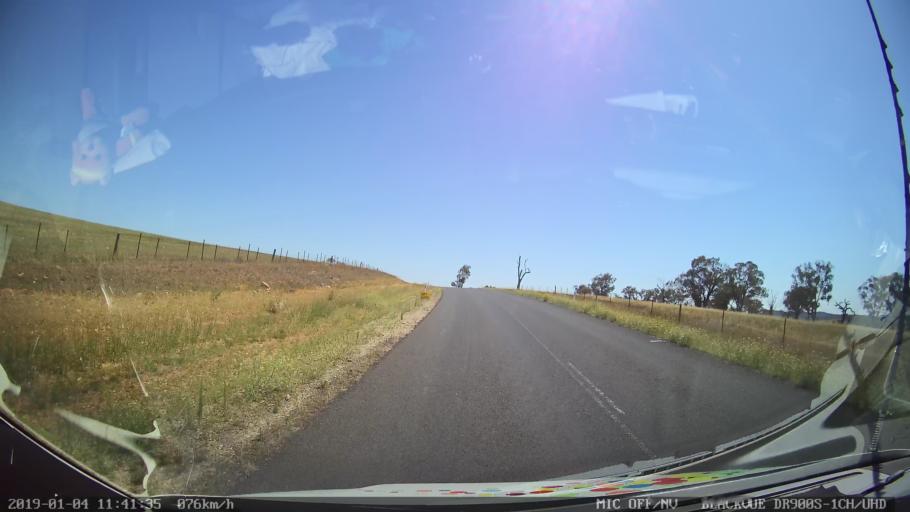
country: AU
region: New South Wales
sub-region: Cabonne
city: Molong
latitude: -32.9921
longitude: 148.7878
